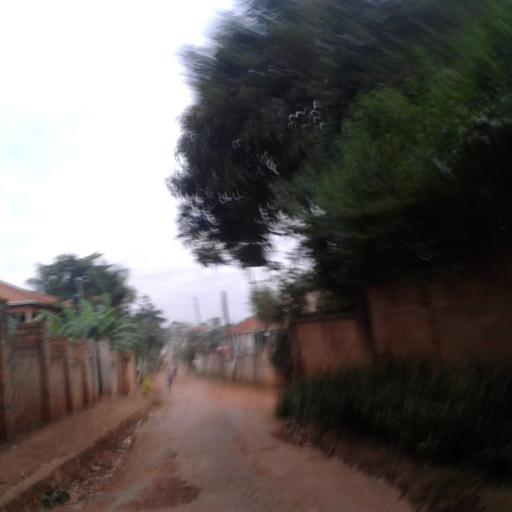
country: UG
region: Central Region
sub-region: Kampala District
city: Kampala
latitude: 0.2464
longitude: 32.6223
